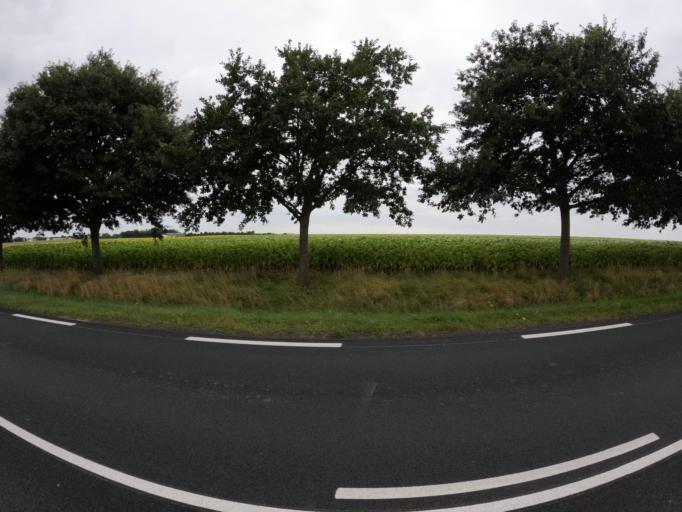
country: FR
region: Pays de la Loire
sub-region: Departement de la Vendee
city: Le Langon
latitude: 46.4930
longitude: -0.9126
